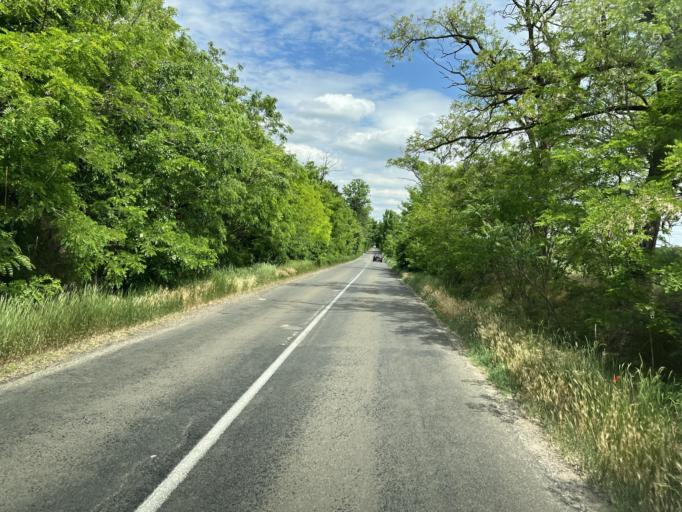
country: HU
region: Pest
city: Toalmas
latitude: 47.4878
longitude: 19.6417
